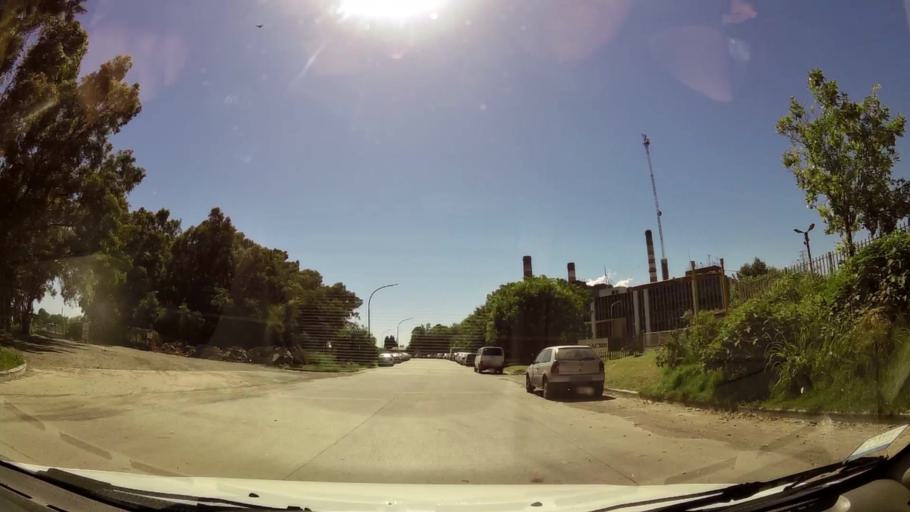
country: AR
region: Buenos Aires F.D.
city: Buenos Aires
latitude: -34.6241
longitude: -58.3442
